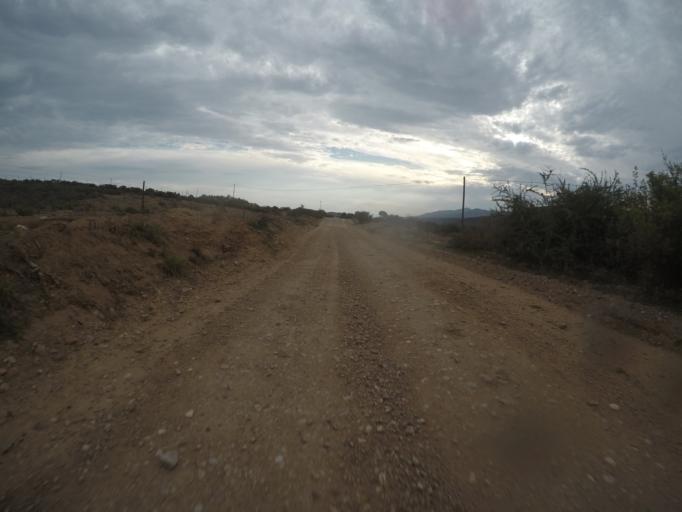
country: ZA
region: Eastern Cape
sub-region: Cacadu District Municipality
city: Willowmore
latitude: -33.4914
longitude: 23.5974
